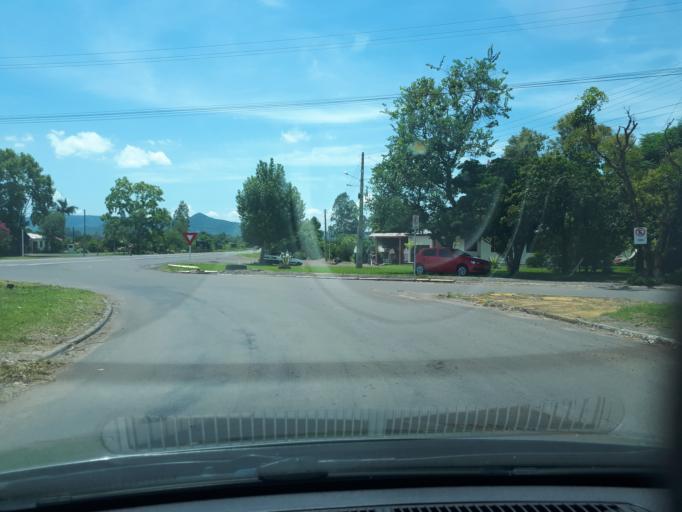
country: BR
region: Rio Grande do Sul
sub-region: Candelaria
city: Candelaria
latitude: -29.7321
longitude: -52.9461
